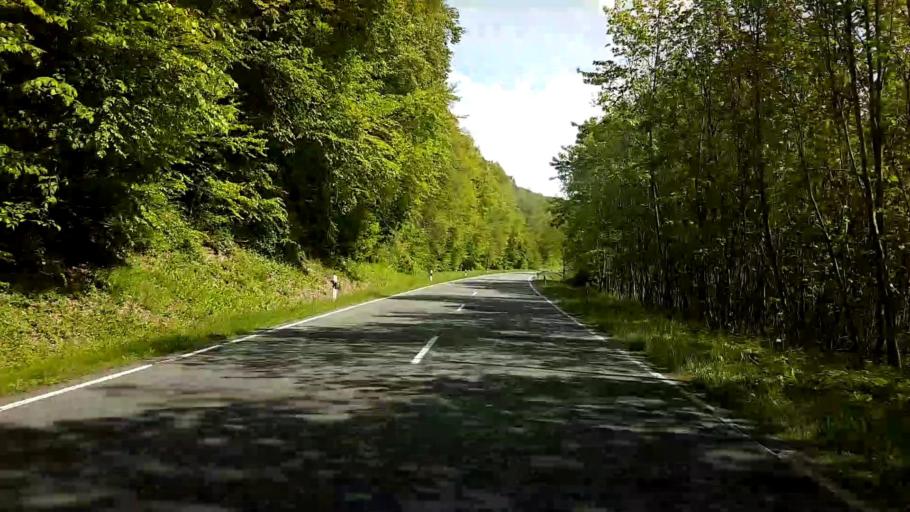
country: DE
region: Bavaria
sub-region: Upper Franconia
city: Ebermannstadt
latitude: 49.7994
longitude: 11.1707
